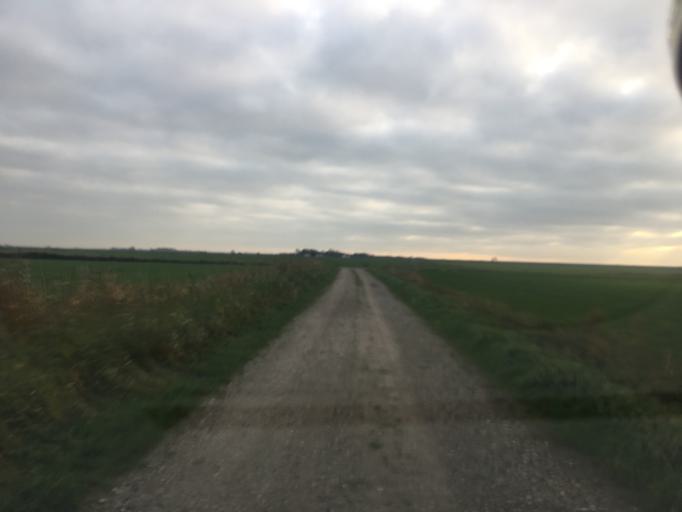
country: DE
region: Schleswig-Holstein
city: Rodenas
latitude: 54.9535
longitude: 8.7367
